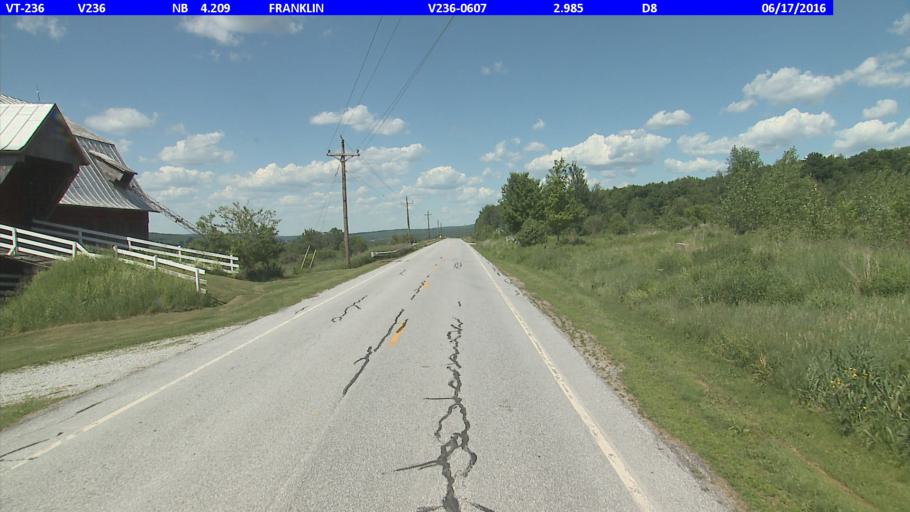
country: US
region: Vermont
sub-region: Franklin County
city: Enosburg Falls
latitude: 44.9697
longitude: -72.8531
